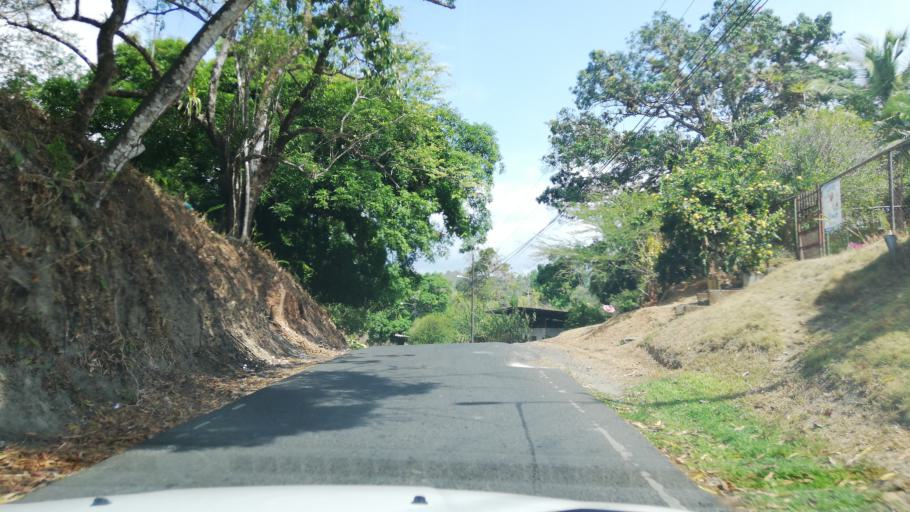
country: PA
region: Panama
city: Alcalde Diaz
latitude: 9.1273
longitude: -79.5658
